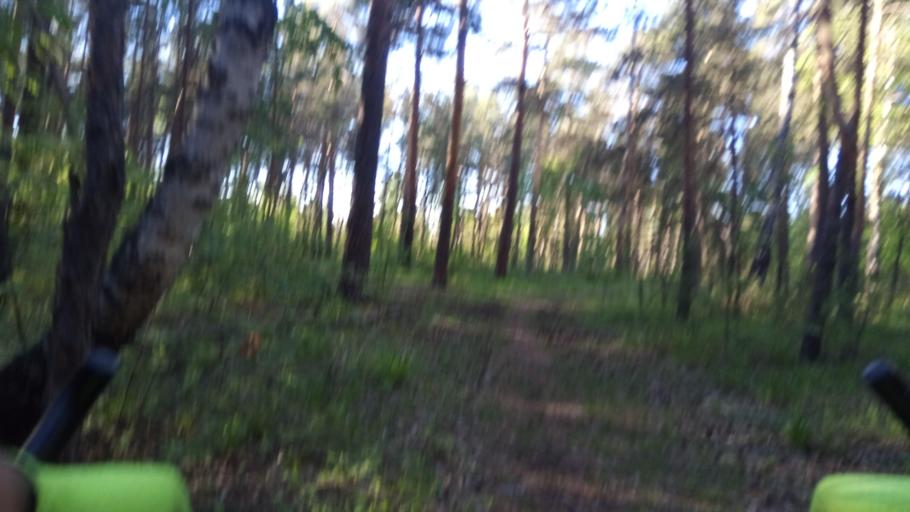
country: RU
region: Chelyabinsk
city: Novosineglazovskiy
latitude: 55.1234
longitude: 61.3431
